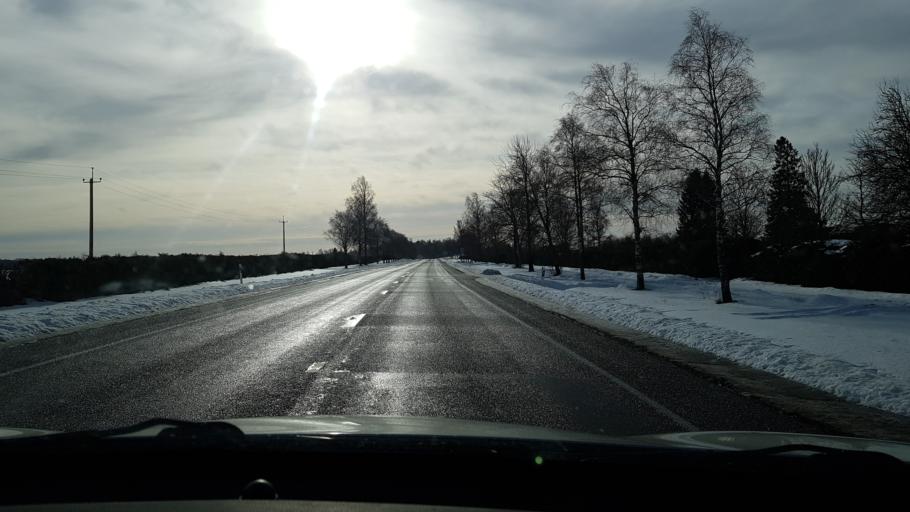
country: EE
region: Jaervamaa
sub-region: Paide linn
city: Paide
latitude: 58.9245
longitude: 25.6127
